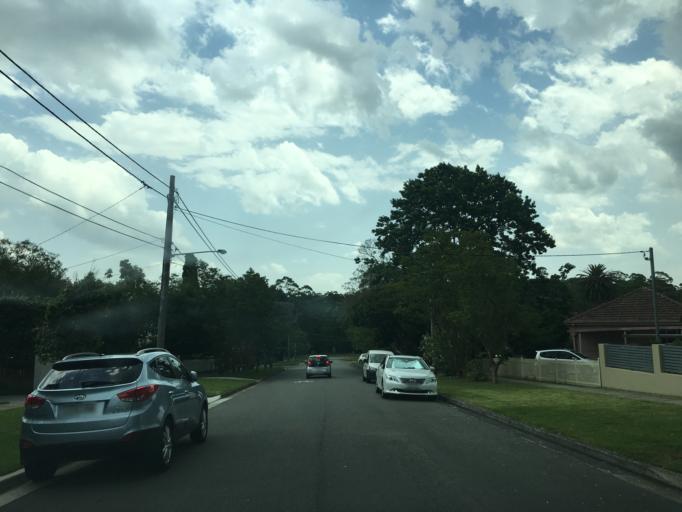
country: AU
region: New South Wales
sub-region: Parramatta
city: Epping
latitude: -33.7831
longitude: 151.0915
